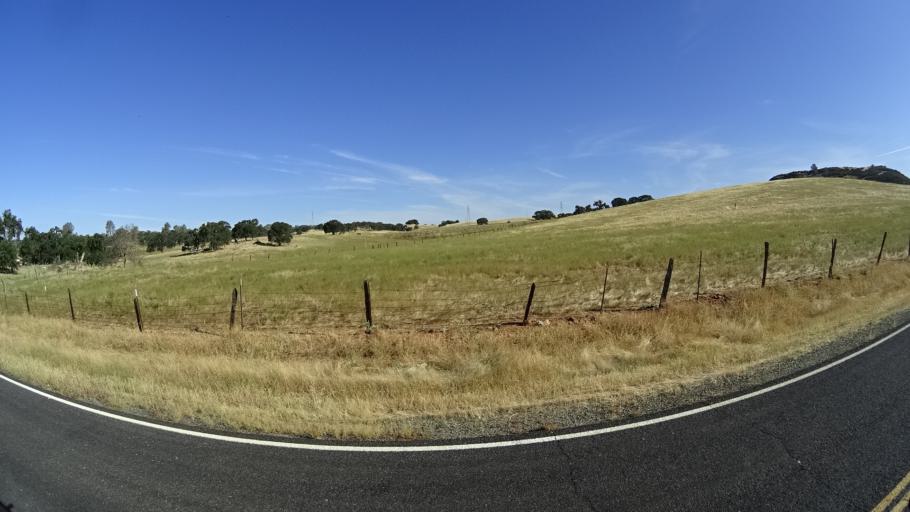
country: US
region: California
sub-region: Calaveras County
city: Valley Springs
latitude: 38.1934
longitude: -120.8051
